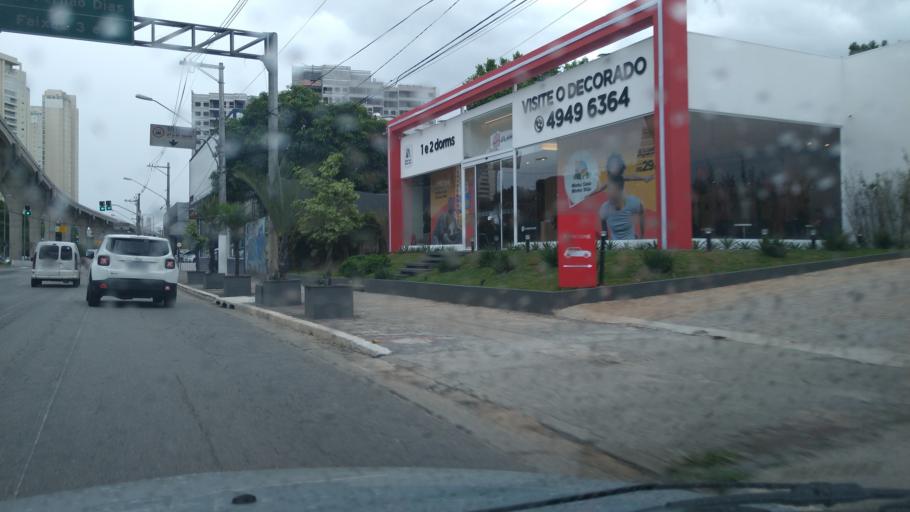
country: BR
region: Sao Paulo
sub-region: Sao Caetano Do Sul
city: Sao Caetano do Sul
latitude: -23.5827
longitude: -46.5667
